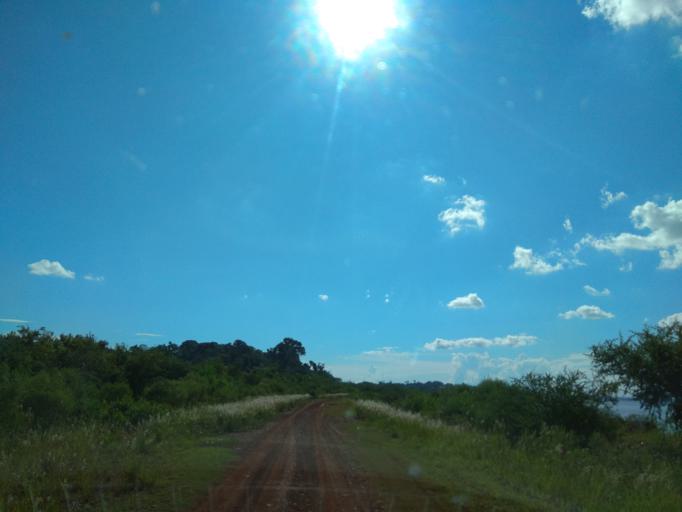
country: AR
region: Misiones
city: Garupa
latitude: -27.4550
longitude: -55.8253
